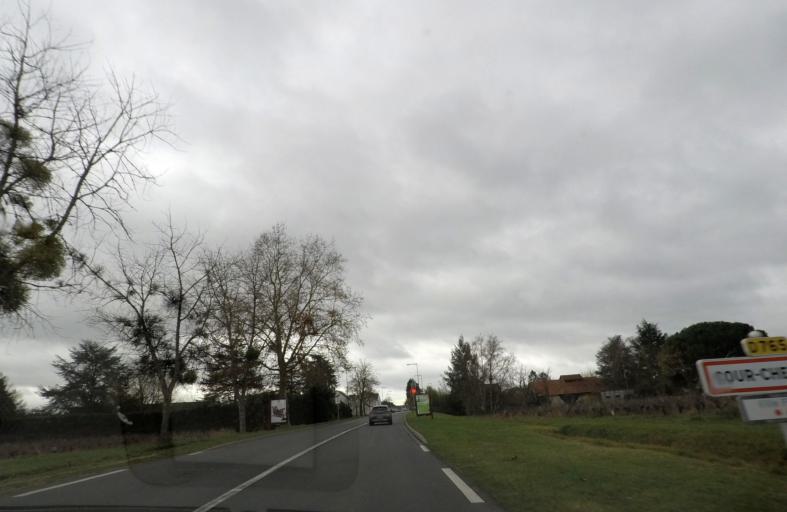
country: FR
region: Centre
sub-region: Departement du Loir-et-Cher
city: Cour-Cheverny
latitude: 47.5155
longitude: 1.4531
